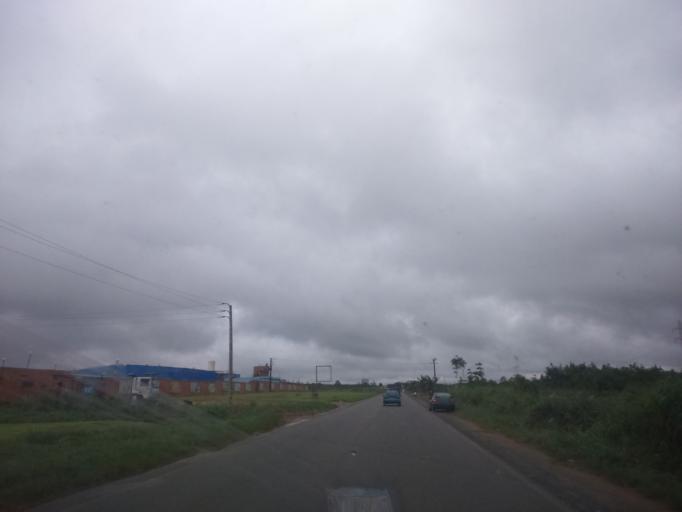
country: CI
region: Sud-Comoe
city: Bonoua
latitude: 5.2754
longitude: -3.5730
